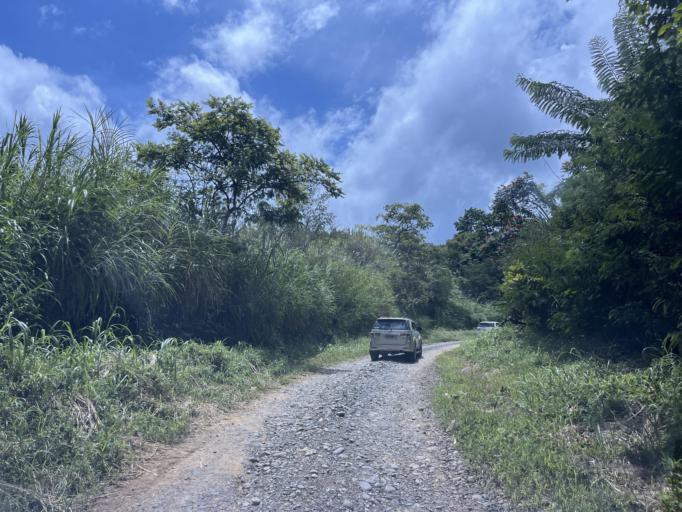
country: PH
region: Northern Mindanao
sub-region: Province of Bukidnon
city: Sumilao
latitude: 8.2990
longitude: 124.9362
